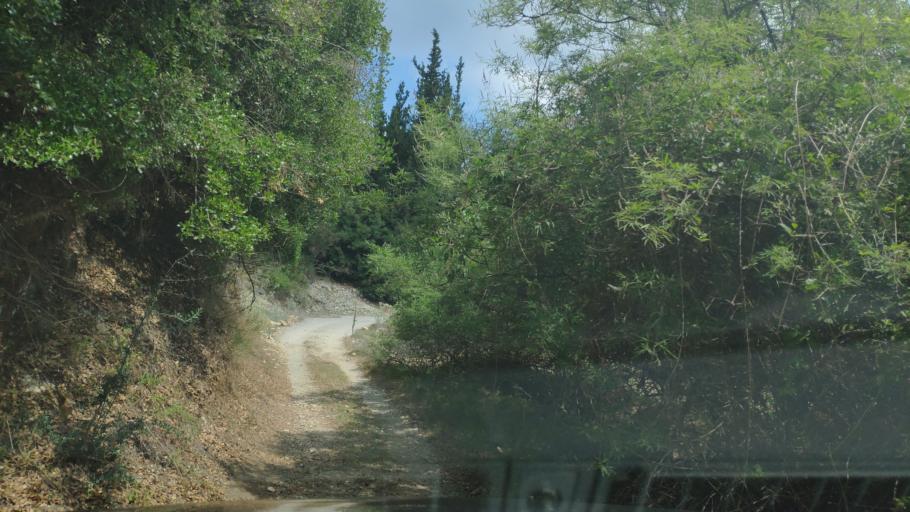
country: GR
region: Ionian Islands
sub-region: Lefkada
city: Lefkada
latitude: 38.8000
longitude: 20.6721
